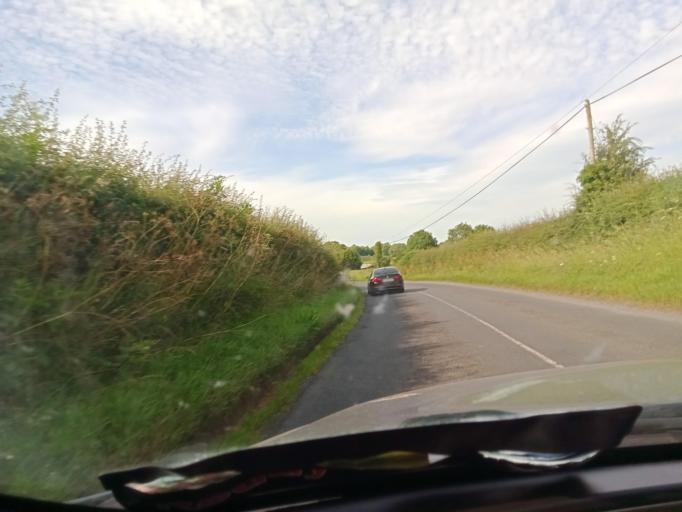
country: IE
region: Leinster
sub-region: An Iarmhi
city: Castlepollard
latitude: 53.7052
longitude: -7.3045
